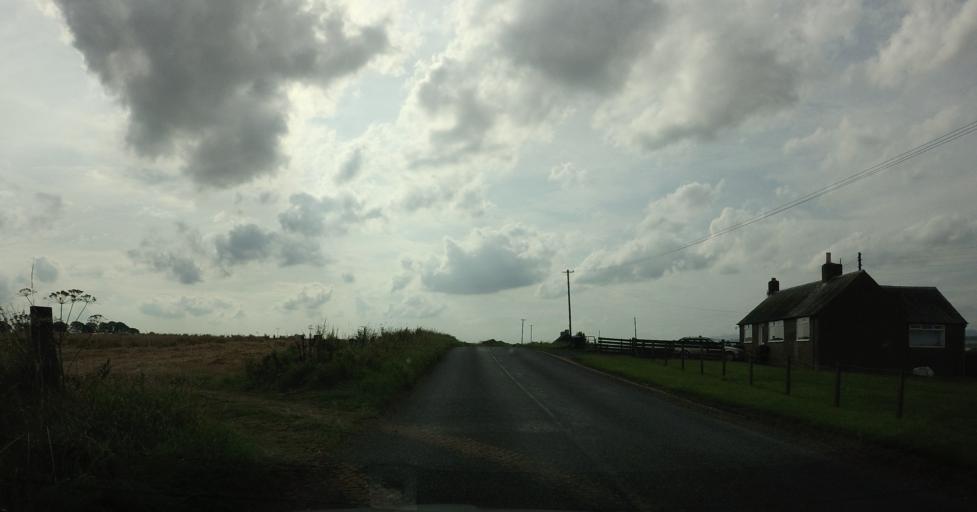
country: GB
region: Scotland
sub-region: Perth and Kinross
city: Methven
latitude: 56.3921
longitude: -3.5744
